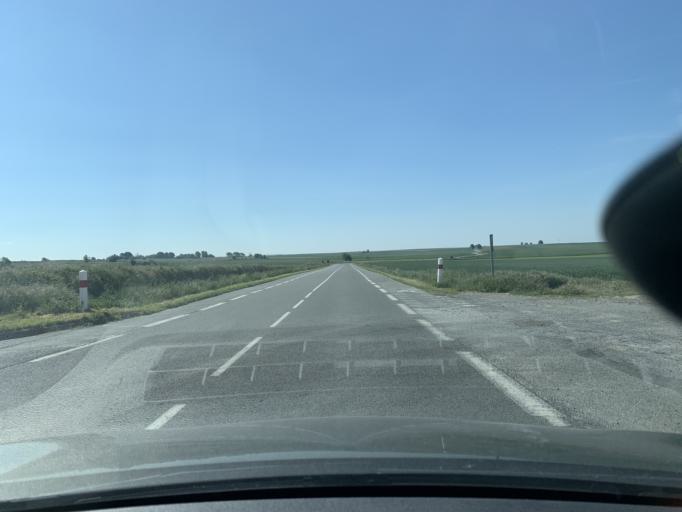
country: FR
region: Nord-Pas-de-Calais
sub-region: Departement du Nord
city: Cambrai
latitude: 50.1404
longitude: 3.2458
